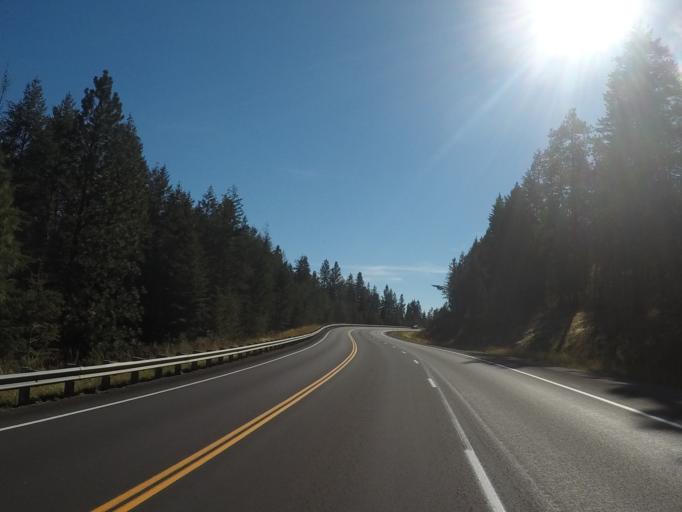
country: US
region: Montana
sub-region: Lake County
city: Polson
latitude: 47.7863
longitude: -114.2395
